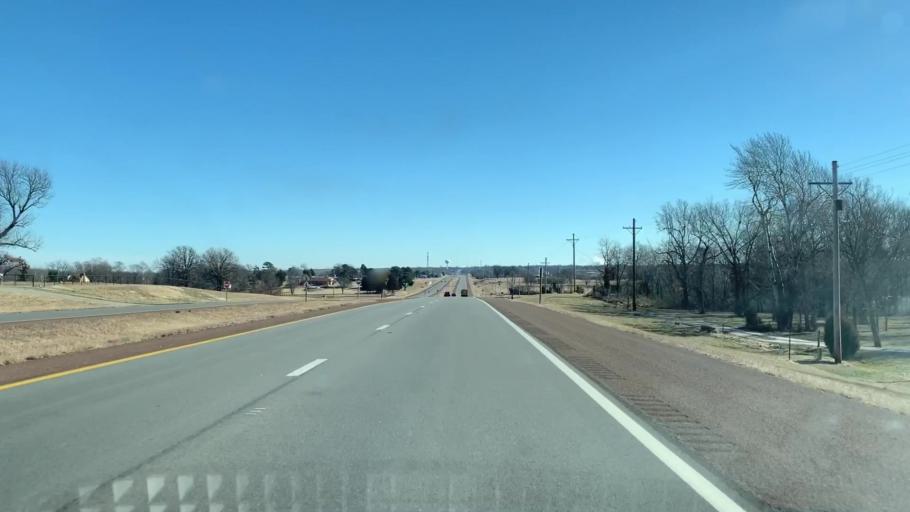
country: US
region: Kansas
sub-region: Cherokee County
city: Galena
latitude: 37.0744
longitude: -94.6709
